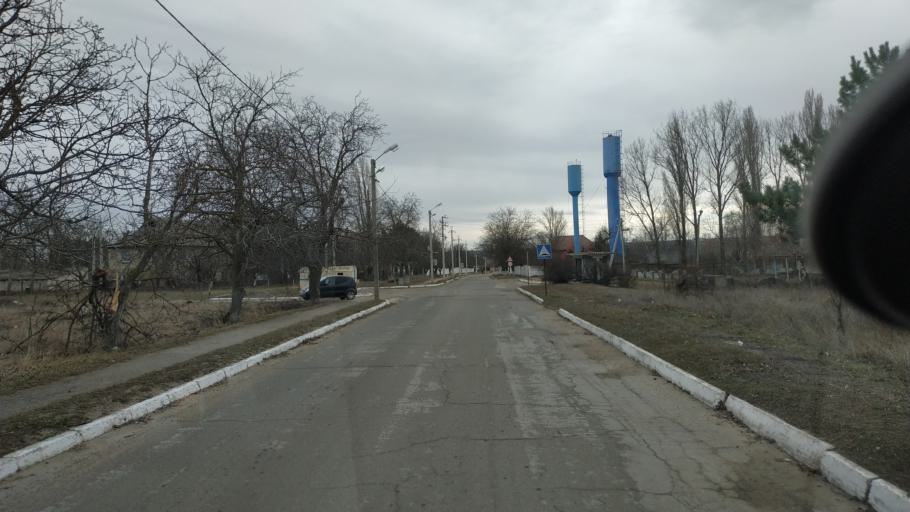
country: MD
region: Telenesti
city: Cocieri
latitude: 47.2949
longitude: 29.1181
